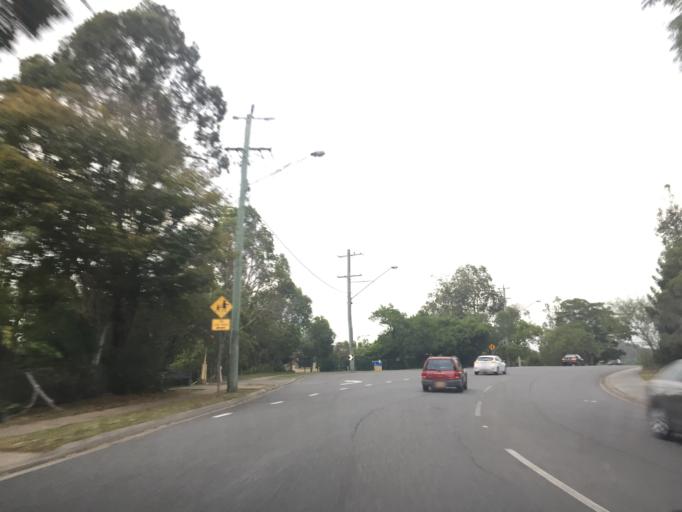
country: AU
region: Queensland
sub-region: Moreton Bay
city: Ferny Hills
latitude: -27.4429
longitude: 152.9411
